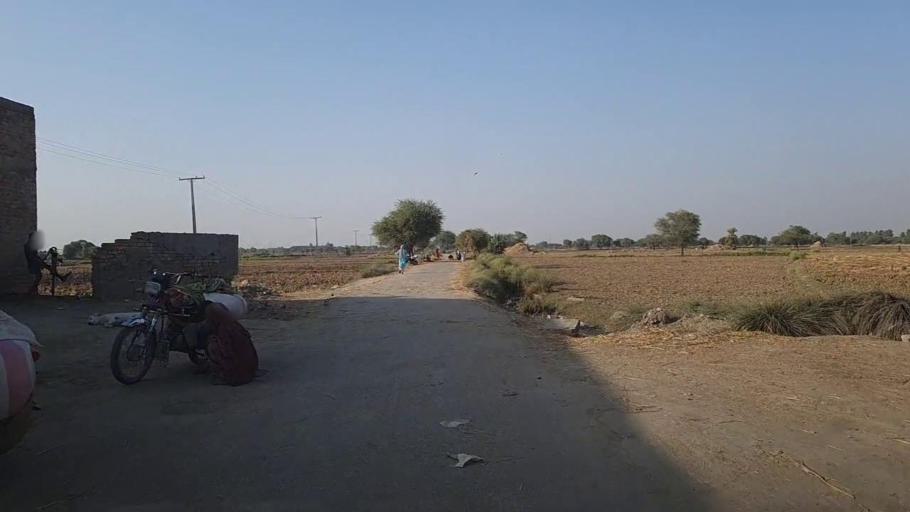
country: PK
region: Sindh
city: Kashmor
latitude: 28.4137
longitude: 69.4112
